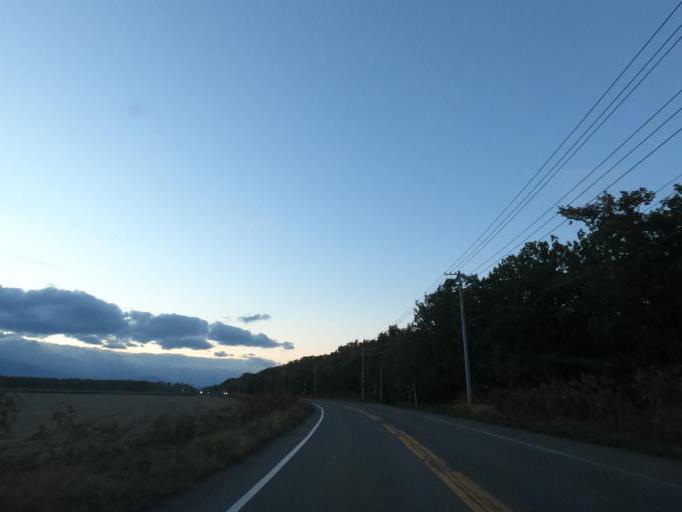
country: JP
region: Hokkaido
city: Obihiro
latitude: 42.6752
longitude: 143.1659
